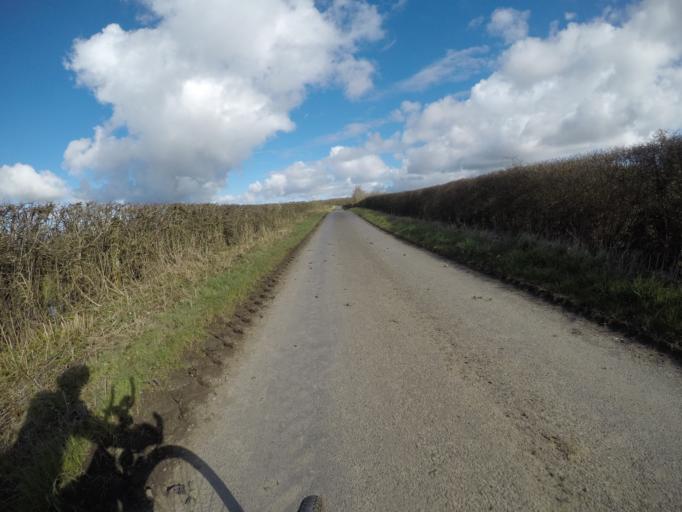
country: GB
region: Scotland
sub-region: North Ayrshire
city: Irvine
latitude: 55.6659
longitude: -4.6503
